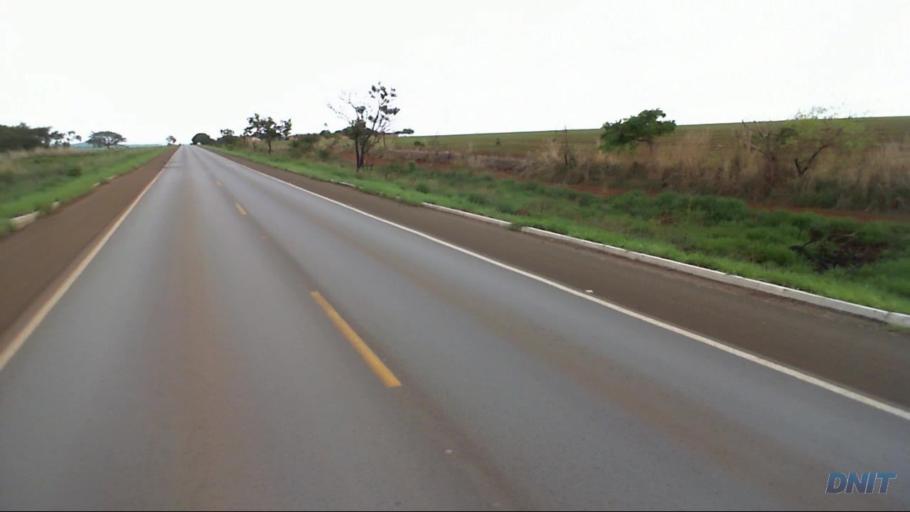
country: BR
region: Goias
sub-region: Barro Alto
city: Barro Alto
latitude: -14.8447
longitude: -49.0282
